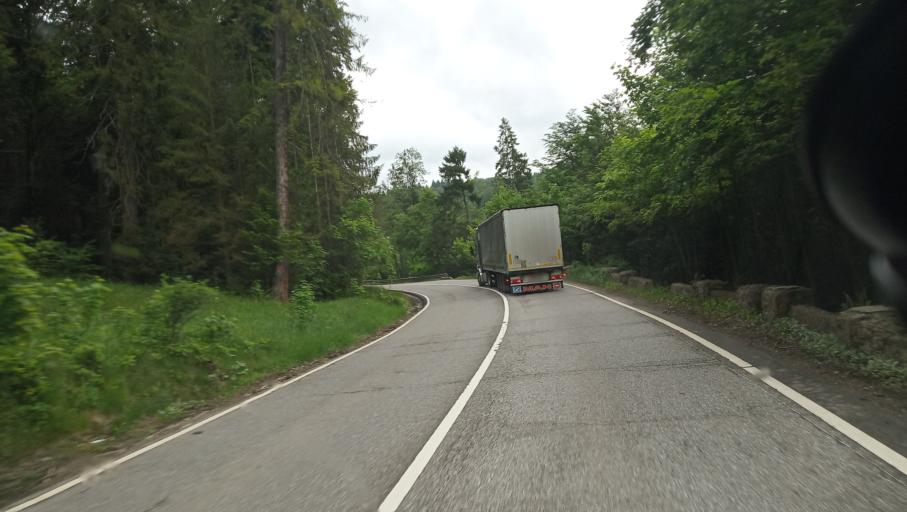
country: RO
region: Neamt
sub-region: Comuna Pipirig
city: Dolhesti
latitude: 47.1631
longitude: 26.0097
